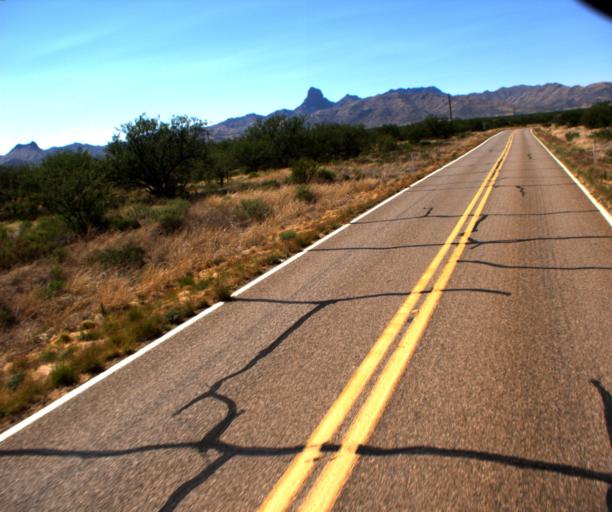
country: US
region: Arizona
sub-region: Pima County
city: Arivaca Junction
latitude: 31.6839
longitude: -111.4864
